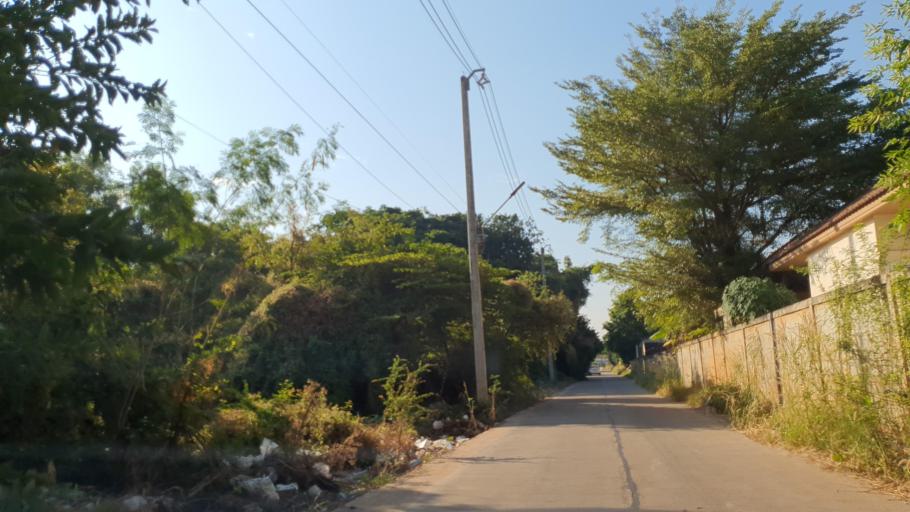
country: TH
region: Khon Kaen
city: Khon Kaen
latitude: 16.4197
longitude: 102.8138
